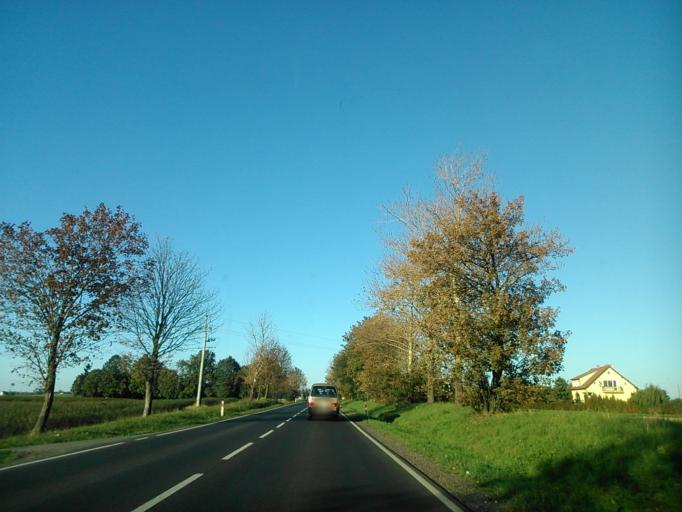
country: PL
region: Kujawsko-Pomorskie
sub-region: Powiat torunski
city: Lubicz Gorny
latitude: 53.0937
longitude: 18.7771
